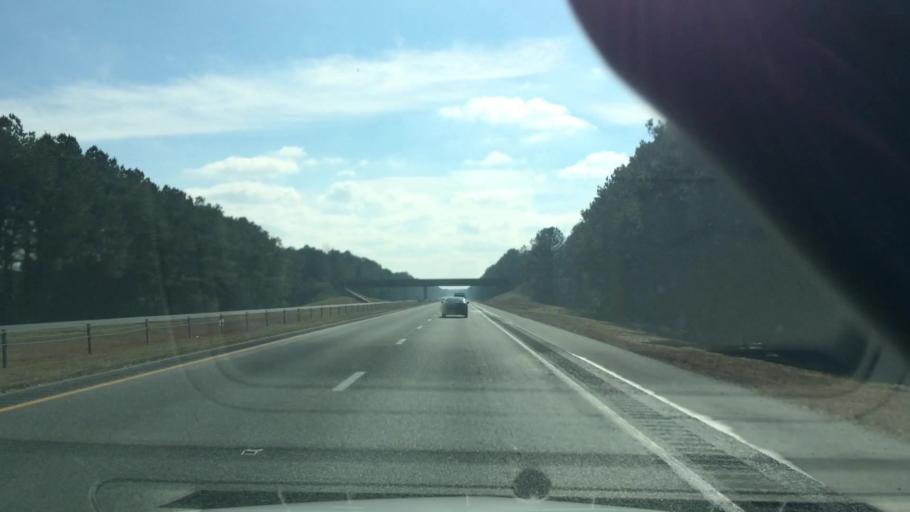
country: US
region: North Carolina
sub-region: Duplin County
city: Wallace
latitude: 34.7345
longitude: -77.9448
